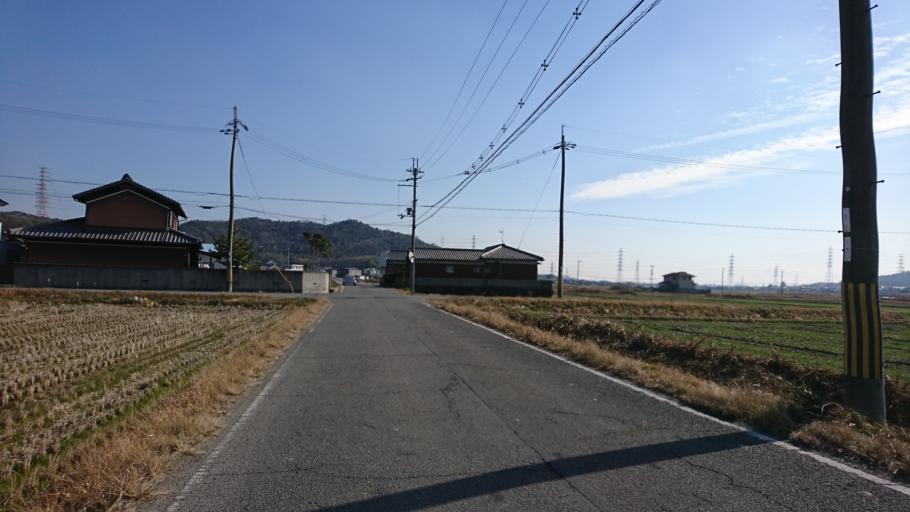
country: JP
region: Hyogo
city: Kakogawacho-honmachi
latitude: 34.8211
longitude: 134.8483
